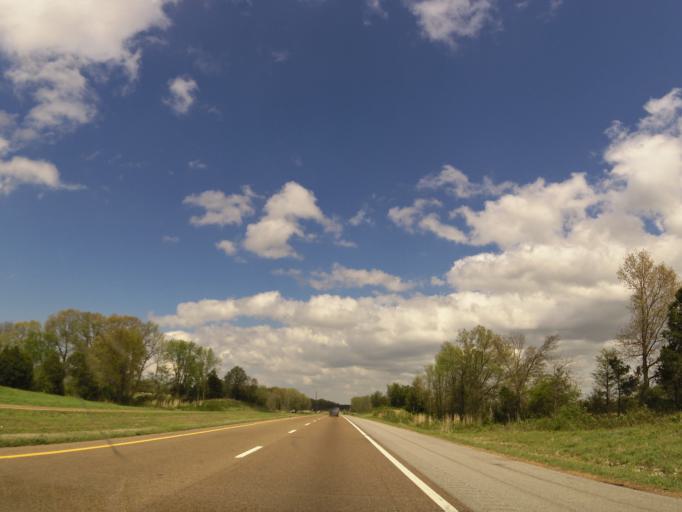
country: US
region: Tennessee
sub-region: Fayette County
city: Hickory Withe
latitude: 35.3236
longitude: -89.5663
